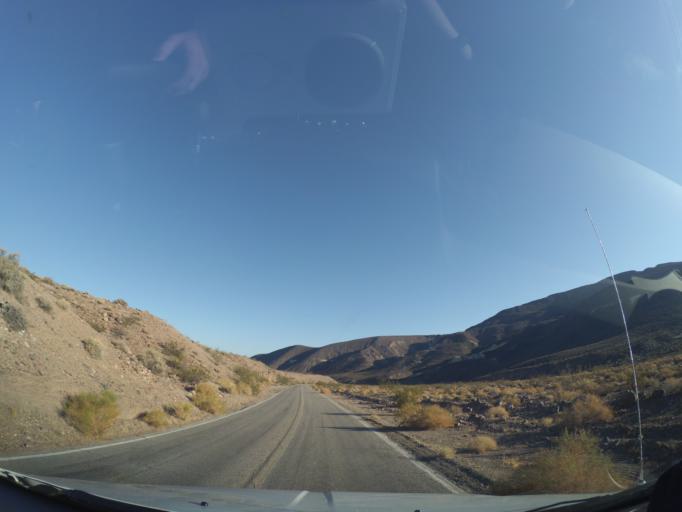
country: US
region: Nevada
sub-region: Nye County
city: Beatty
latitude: 36.2952
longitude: -116.6779
